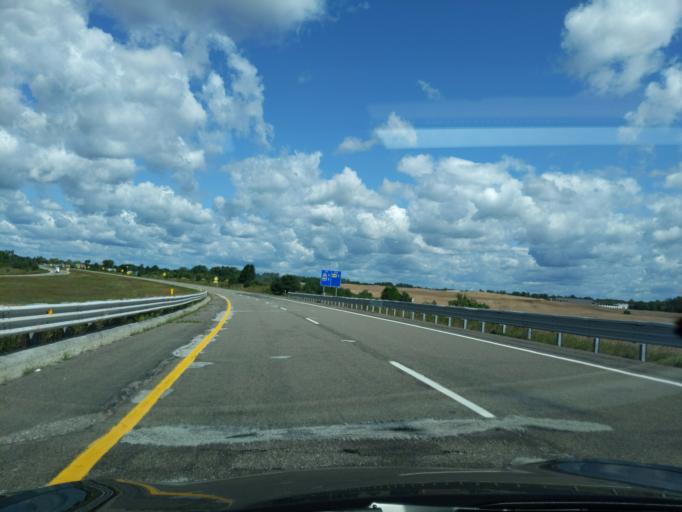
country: US
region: Michigan
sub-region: Clare County
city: Clare
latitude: 43.8025
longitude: -84.7593
